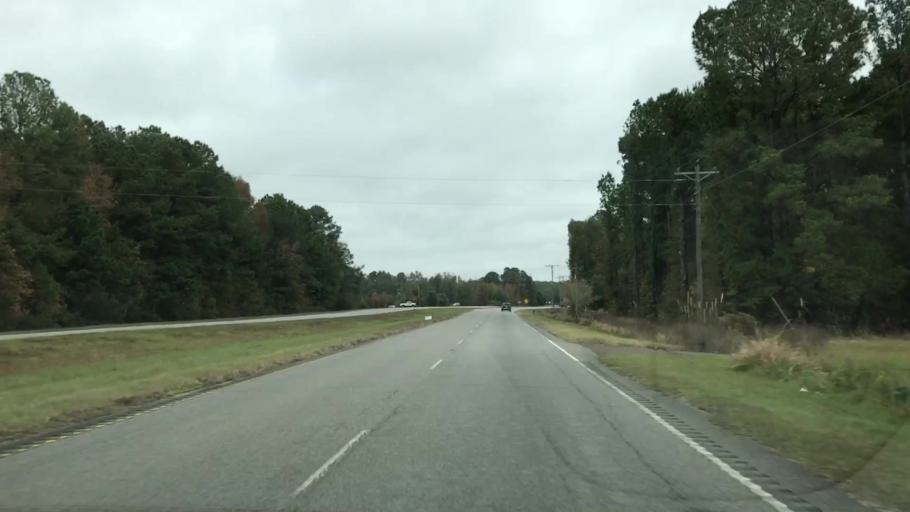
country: US
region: South Carolina
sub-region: Charleston County
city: Awendaw
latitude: 33.0253
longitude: -79.6292
